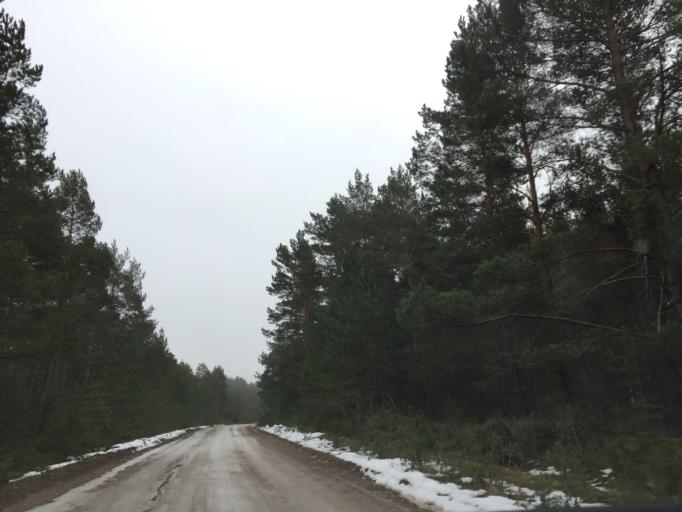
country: EE
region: Saare
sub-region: Kuressaare linn
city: Kuressaare
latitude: 58.4982
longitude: 21.9819
